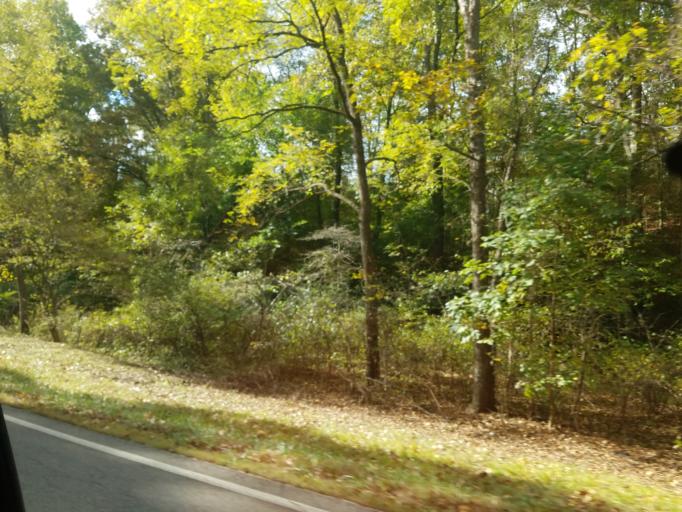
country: US
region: Ohio
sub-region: Vinton County
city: McArthur
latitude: 39.1705
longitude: -82.4402
